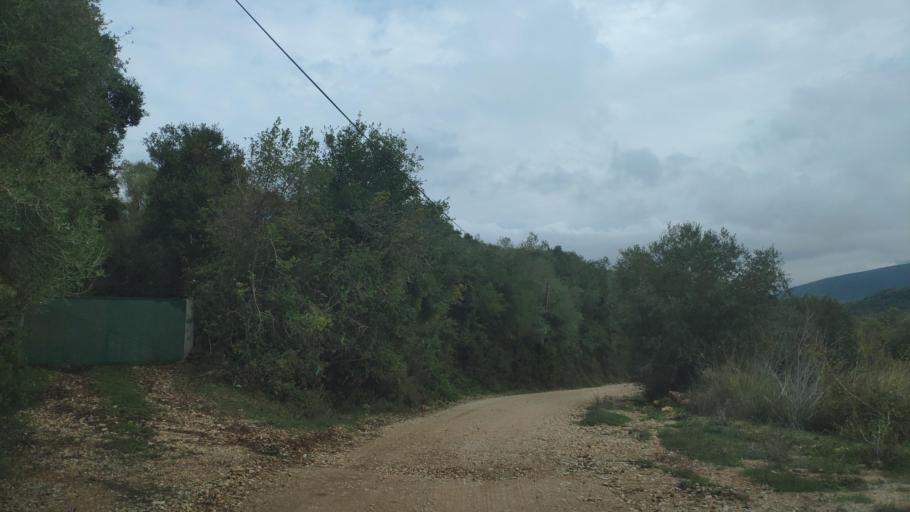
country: GR
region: West Greece
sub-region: Nomos Aitolias kai Akarnanias
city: Vonitsa
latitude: 38.9242
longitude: 20.8654
